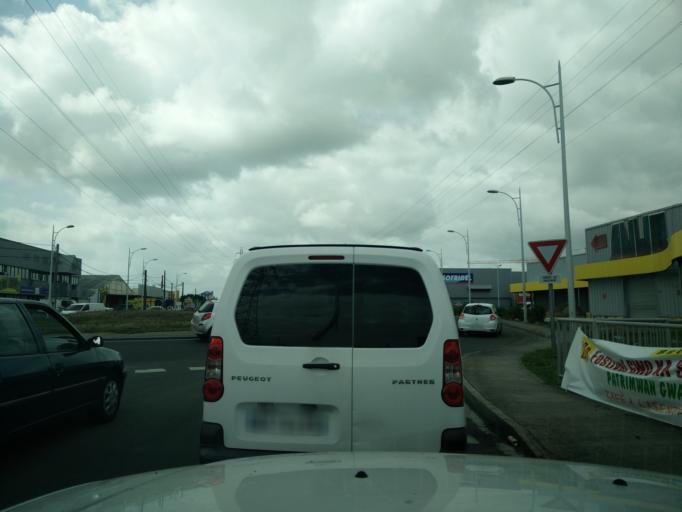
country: GP
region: Guadeloupe
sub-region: Guadeloupe
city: Pointe-a-Pitre
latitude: 16.2422
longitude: -61.5551
